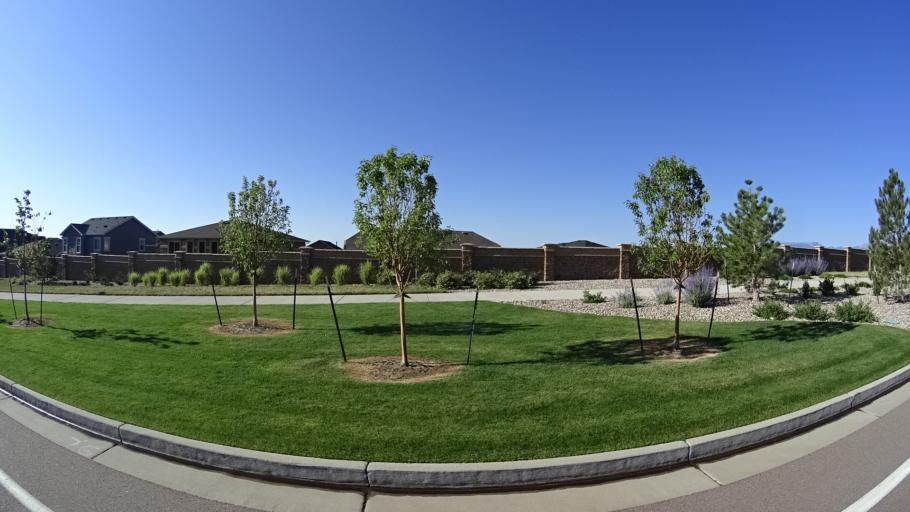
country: US
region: Colorado
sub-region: El Paso County
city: Black Forest
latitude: 38.9711
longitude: -104.7312
